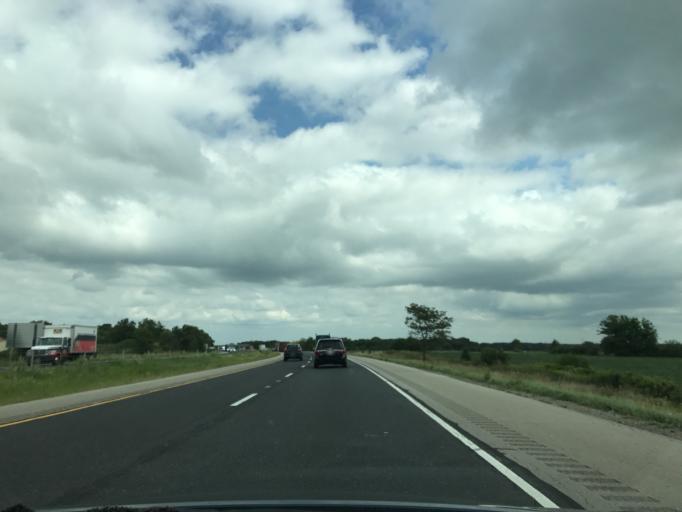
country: US
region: Illinois
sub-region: Grundy County
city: Minooka
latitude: 41.4650
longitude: -88.2467
